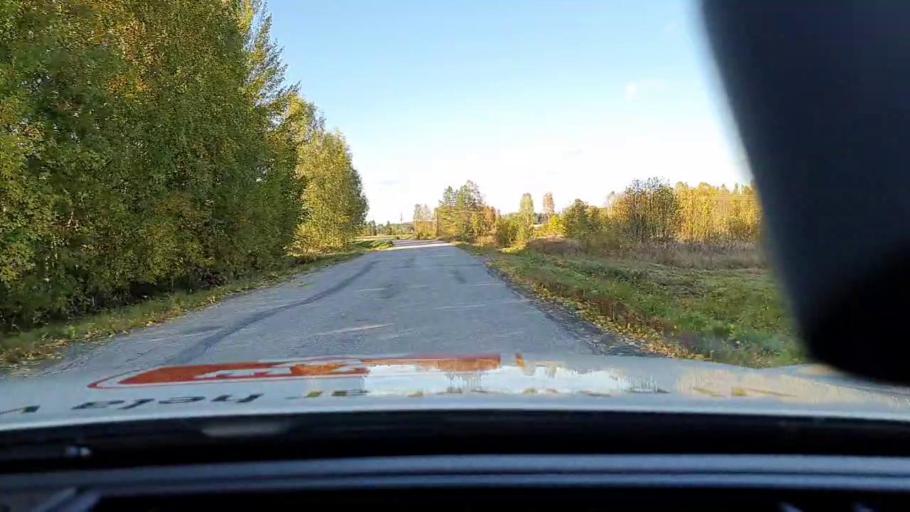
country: SE
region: Norrbotten
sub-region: Pitea Kommun
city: Norrfjarden
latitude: 65.5187
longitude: 21.4948
